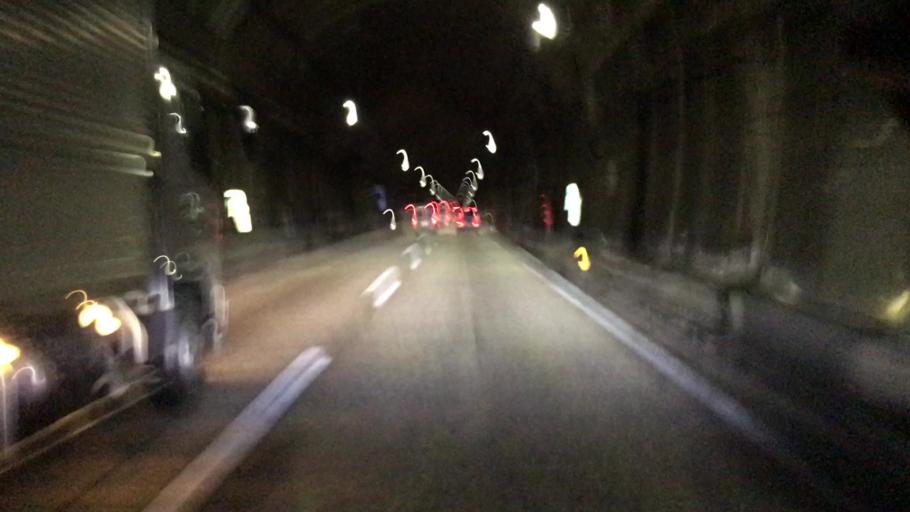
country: JP
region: Hyogo
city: Kobe
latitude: 34.7278
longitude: 135.1813
